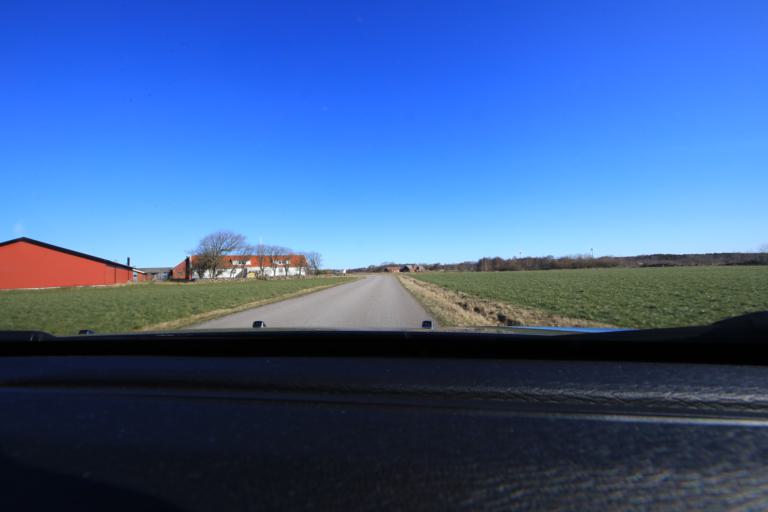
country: SE
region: Halland
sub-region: Varbergs Kommun
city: Traslovslage
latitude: 57.0484
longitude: 12.3311
